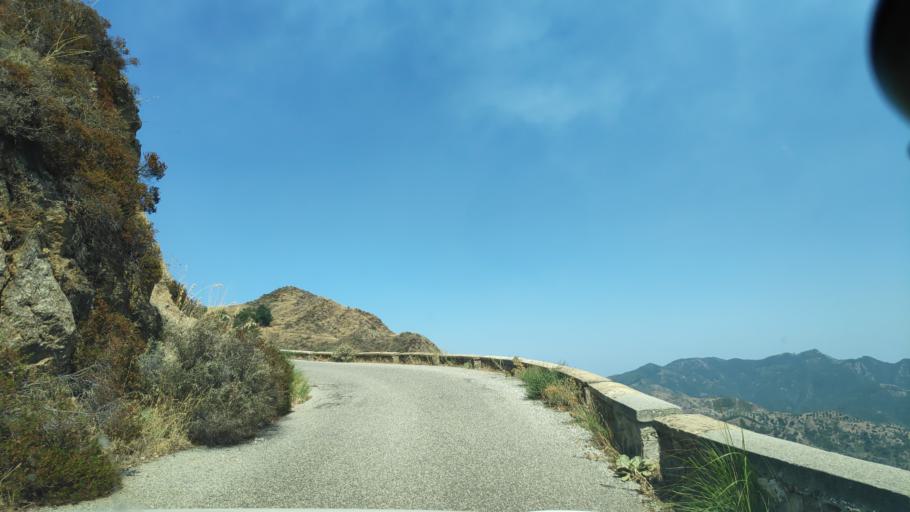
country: IT
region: Calabria
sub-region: Provincia di Reggio Calabria
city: Bova
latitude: 38.0017
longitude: 15.9293
